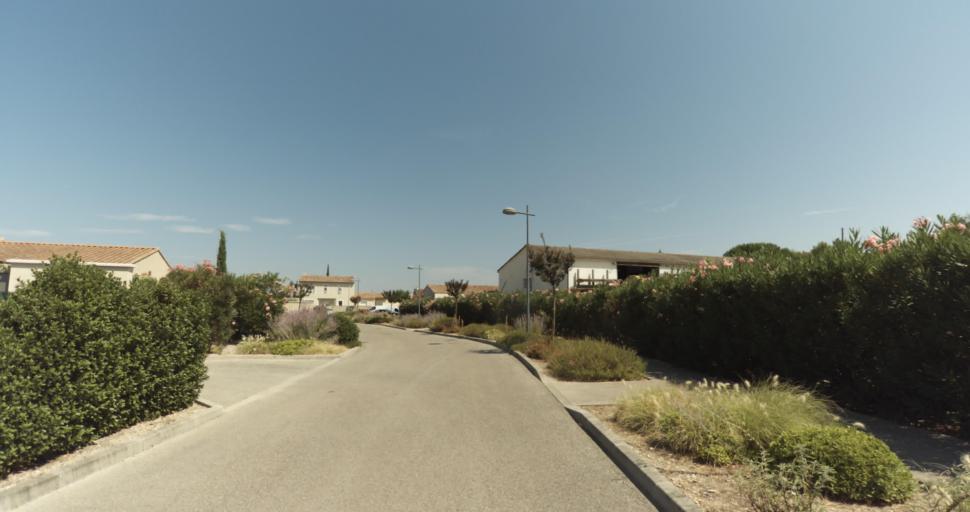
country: FR
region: Provence-Alpes-Cote d'Azur
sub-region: Departement du Vaucluse
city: Monteux
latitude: 44.0323
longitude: 4.9849
